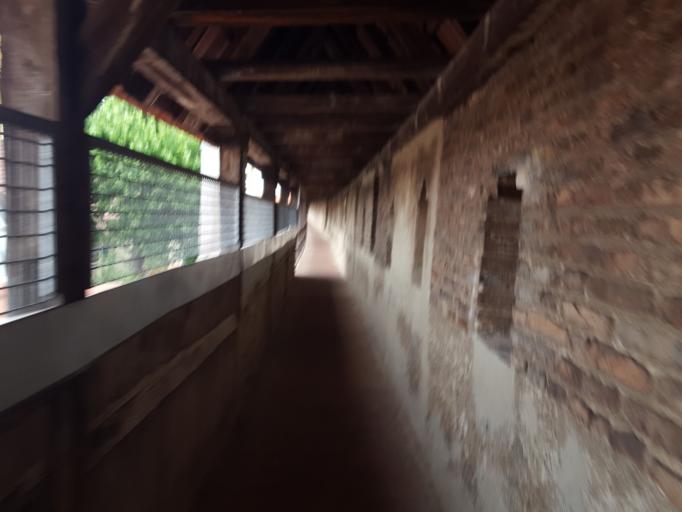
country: DE
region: Bavaria
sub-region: Swabia
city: Noerdlingen
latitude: 48.8531
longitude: 10.4939
